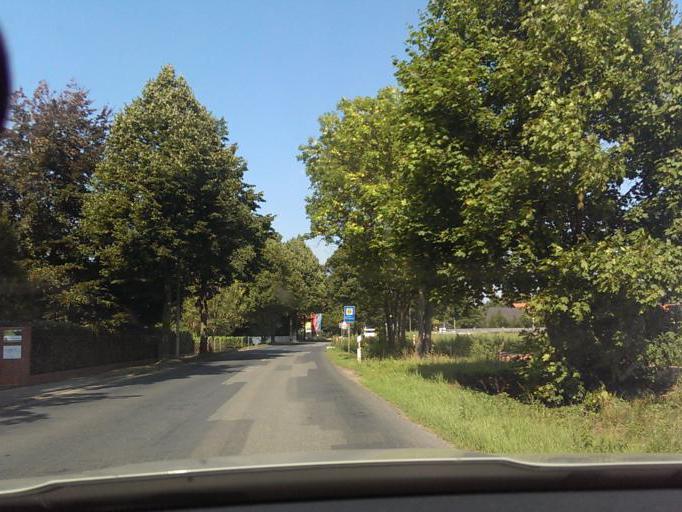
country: DE
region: Lower Saxony
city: Isernhagen Farster Bauerschaft
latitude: 52.4695
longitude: 9.7912
